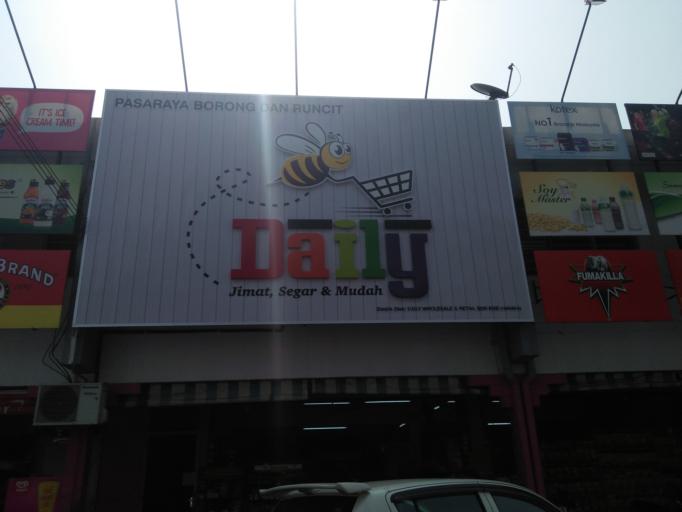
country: MY
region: Kedah
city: Kulim
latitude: 5.3726
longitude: 100.5579
